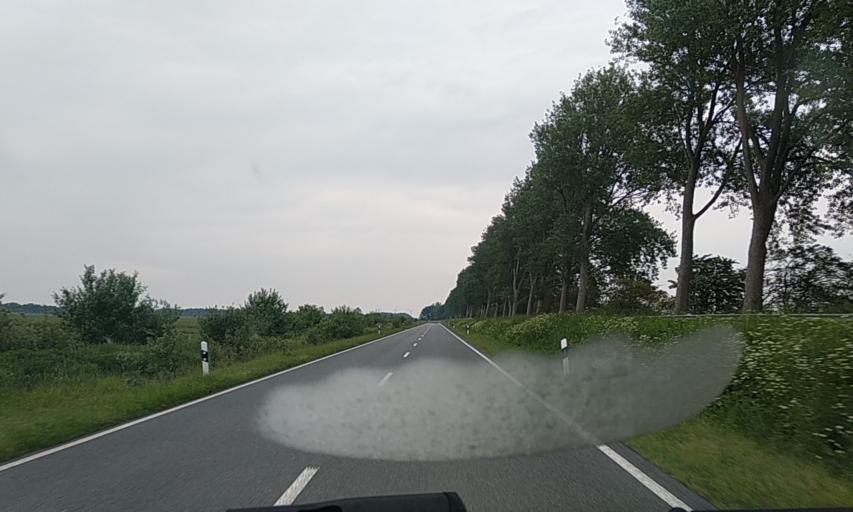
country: DE
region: Schleswig-Holstein
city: Meggerdorf
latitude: 54.3282
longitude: 9.3933
